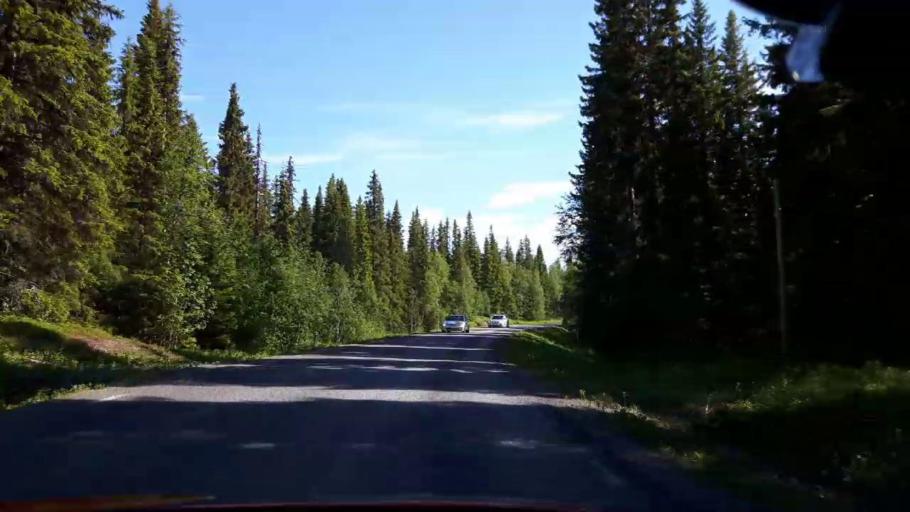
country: SE
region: Jaemtland
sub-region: Krokoms Kommun
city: Valla
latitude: 63.7372
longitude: 14.1193
